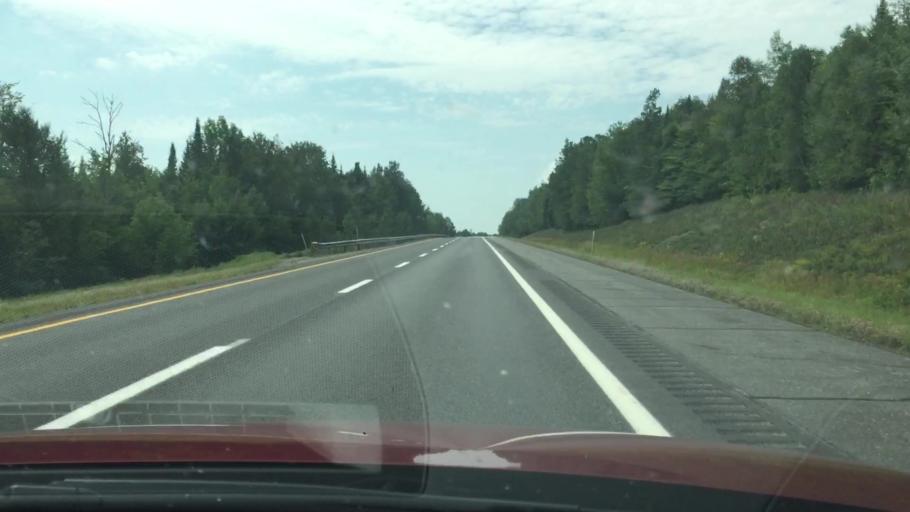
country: US
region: Maine
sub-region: Aroostook County
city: Hodgdon
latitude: 46.1272
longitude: -68.1018
